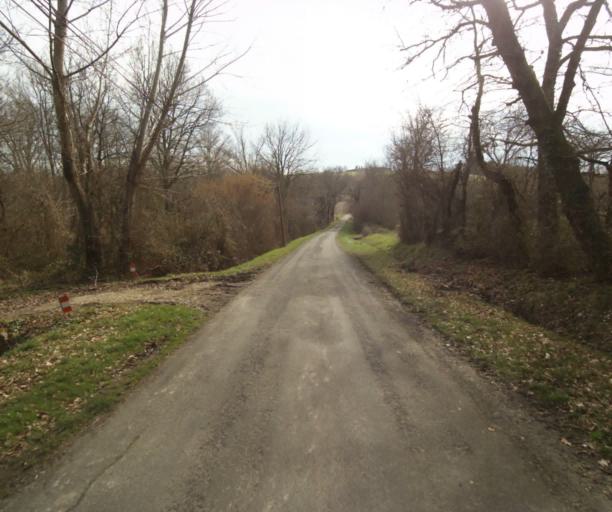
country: FR
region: Aquitaine
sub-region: Departement des Landes
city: Gabarret
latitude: 43.9434
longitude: 0.0466
